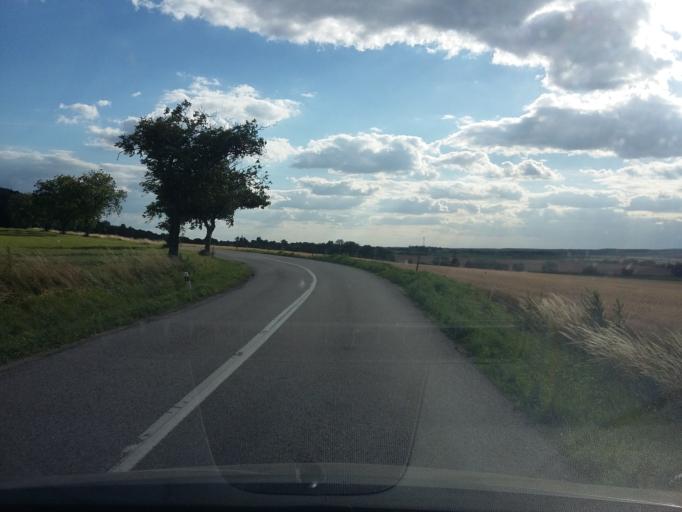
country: SK
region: Trnavsky
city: Smolenice
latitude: 48.5435
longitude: 17.3456
